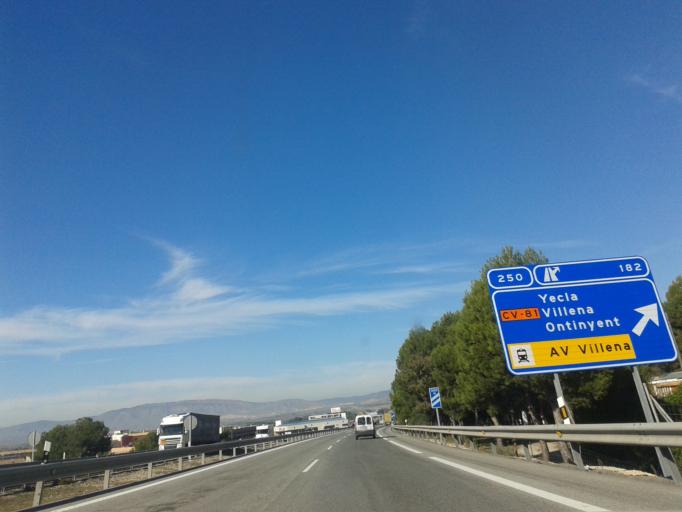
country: ES
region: Valencia
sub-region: Provincia de Alicante
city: Villena
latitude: 38.6415
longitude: -0.8630
